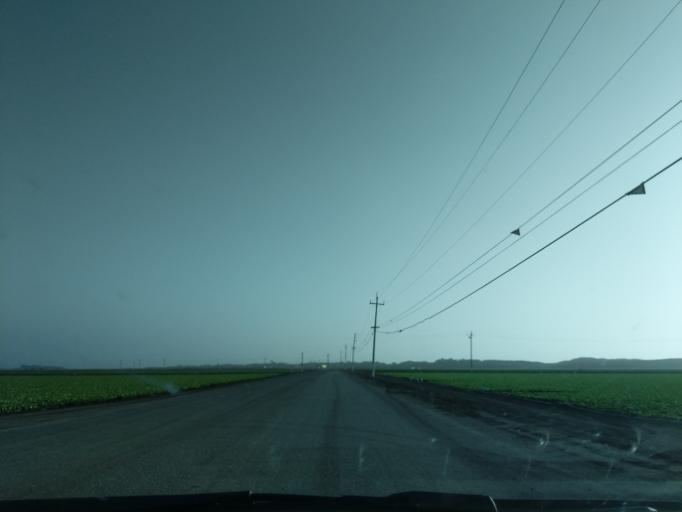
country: US
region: California
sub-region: Monterey County
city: Castroville
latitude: 36.7768
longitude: -121.7836
